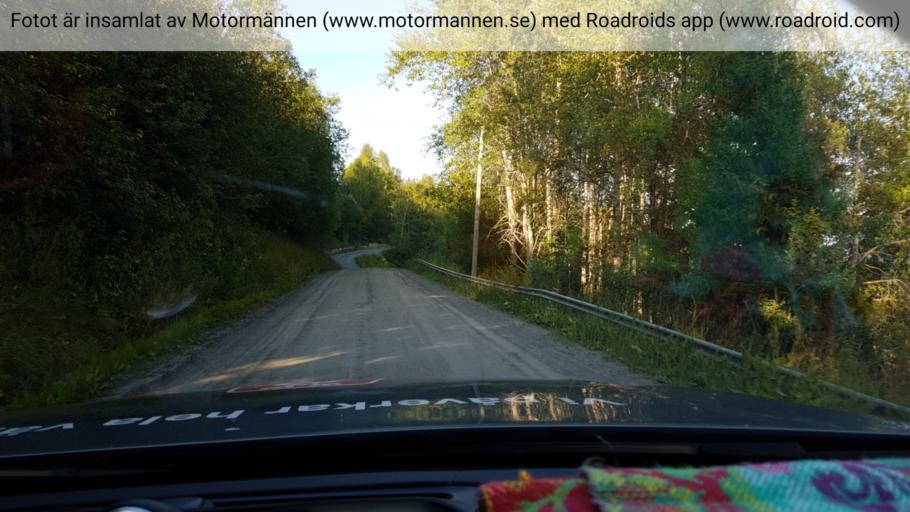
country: SE
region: Jaemtland
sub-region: Are Kommun
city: Jarpen
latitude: 63.3152
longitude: 13.3361
